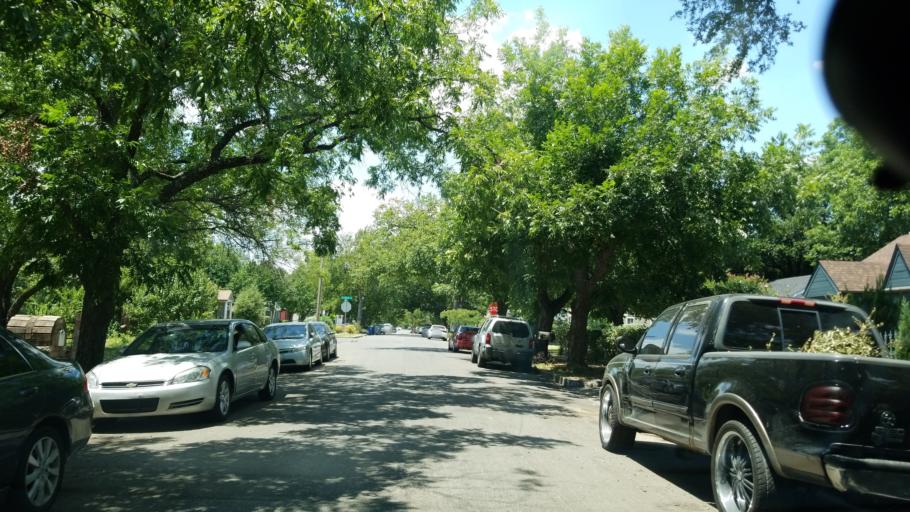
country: US
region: Texas
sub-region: Dallas County
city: Cockrell Hill
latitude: 32.7223
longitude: -96.8414
